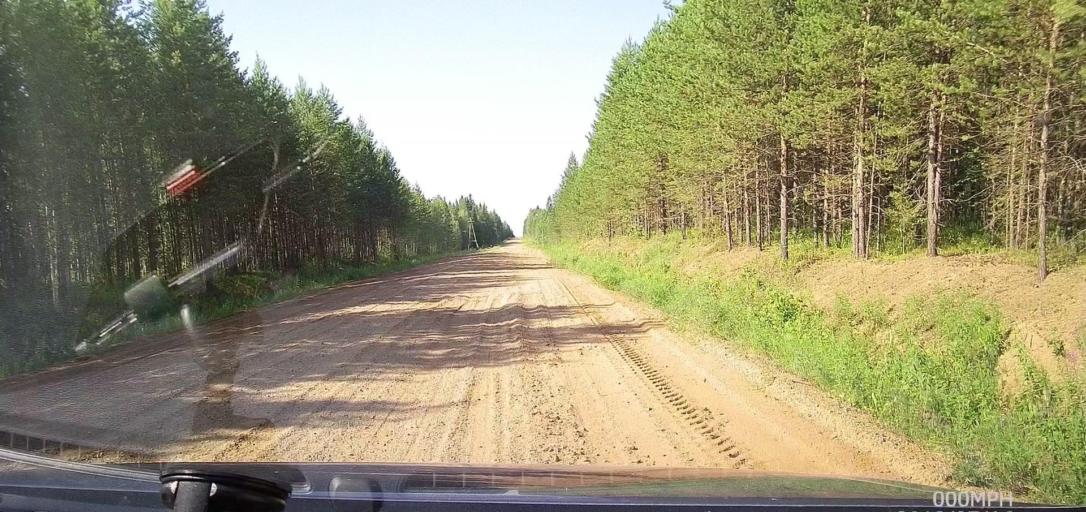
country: RU
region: Arkhangelskaya
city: Mezen'
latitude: 65.4488
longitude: 45.0355
